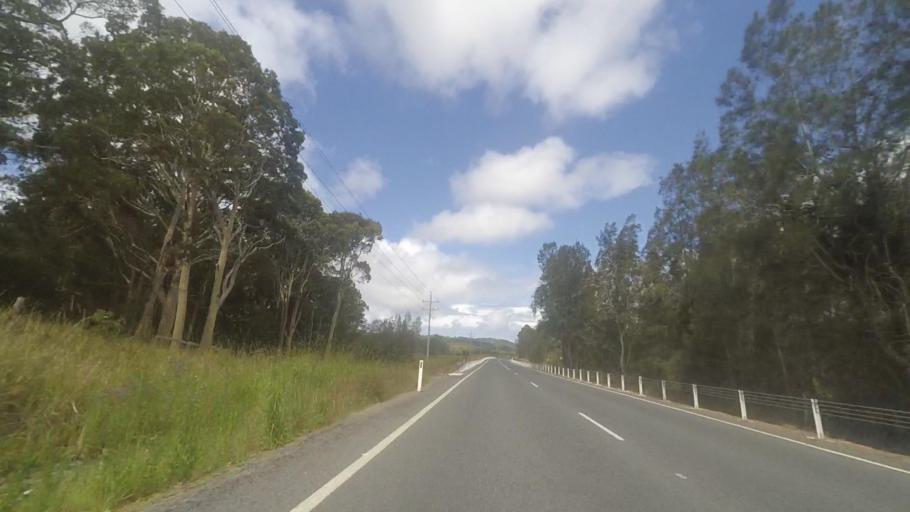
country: AU
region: New South Wales
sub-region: Great Lakes
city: Bulahdelah
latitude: -32.3850
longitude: 152.4025
